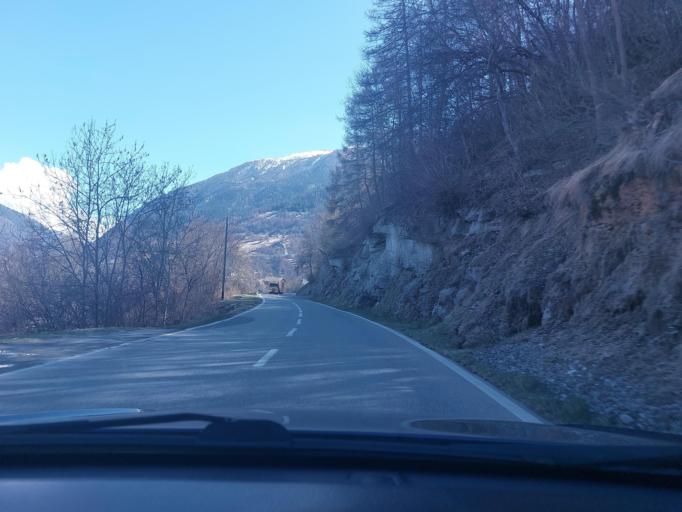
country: CH
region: Valais
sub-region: Herens District
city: Heremence
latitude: 46.1837
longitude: 7.4104
